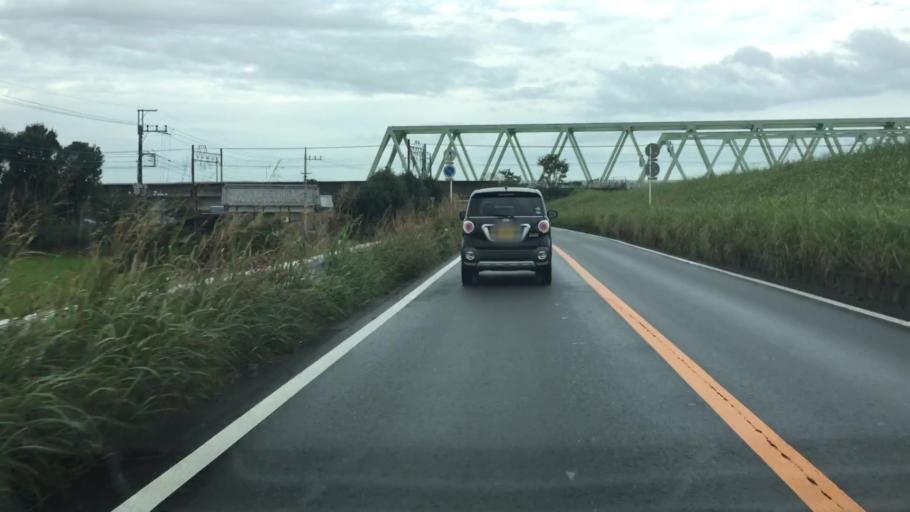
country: JP
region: Ibaraki
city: Toride
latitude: 35.8843
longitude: 140.0577
